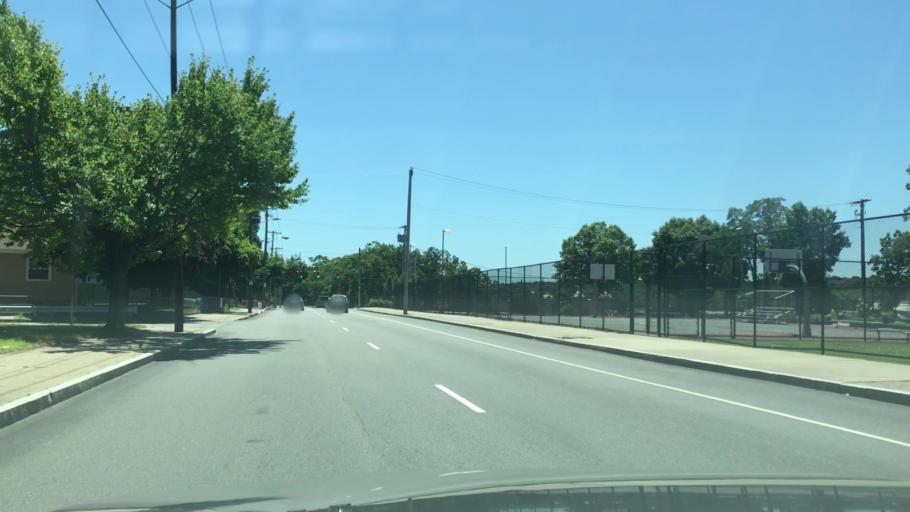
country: US
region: Rhode Island
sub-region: Providence County
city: Pawtucket
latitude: 41.8655
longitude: -71.3757
